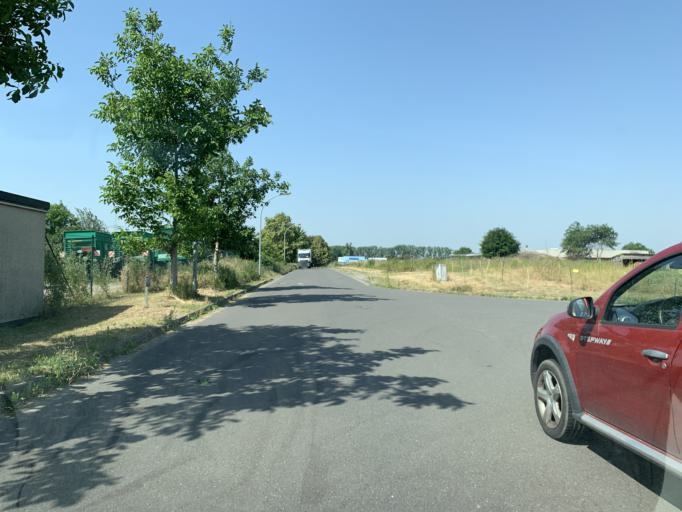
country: DE
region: Saxony-Anhalt
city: Erxleben
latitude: 52.2144
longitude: 11.2463
